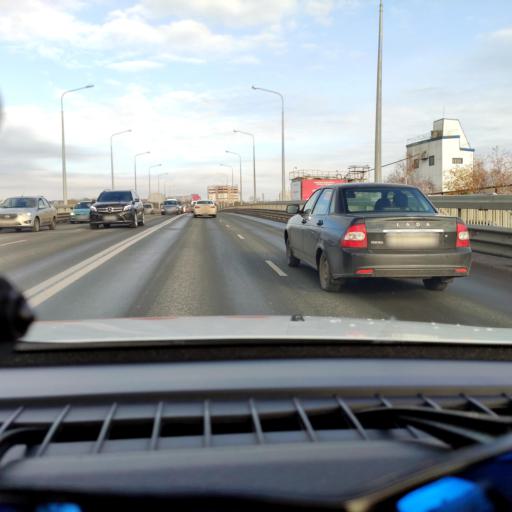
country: RU
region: Samara
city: Samara
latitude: 53.1743
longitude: 50.1935
